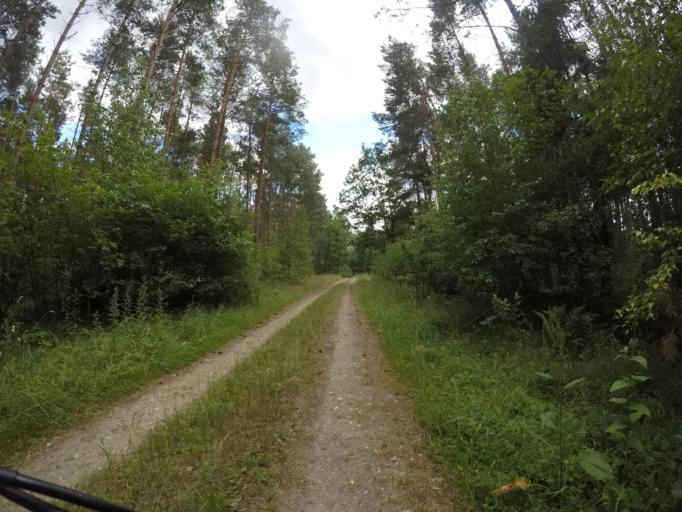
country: DE
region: Mecklenburg-Vorpommern
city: Lubtheen
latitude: 53.2752
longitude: 10.9969
